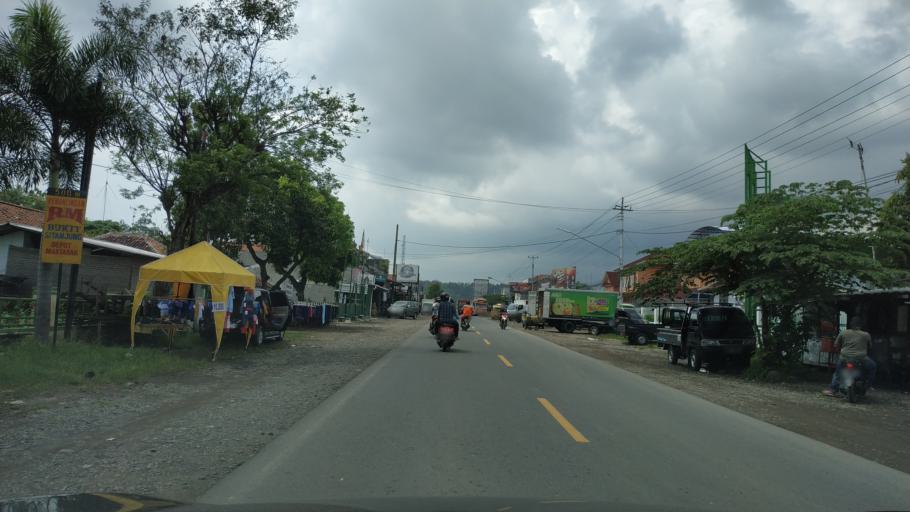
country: ID
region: Central Java
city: Lebaksiu
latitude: -7.0463
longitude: 109.1403
